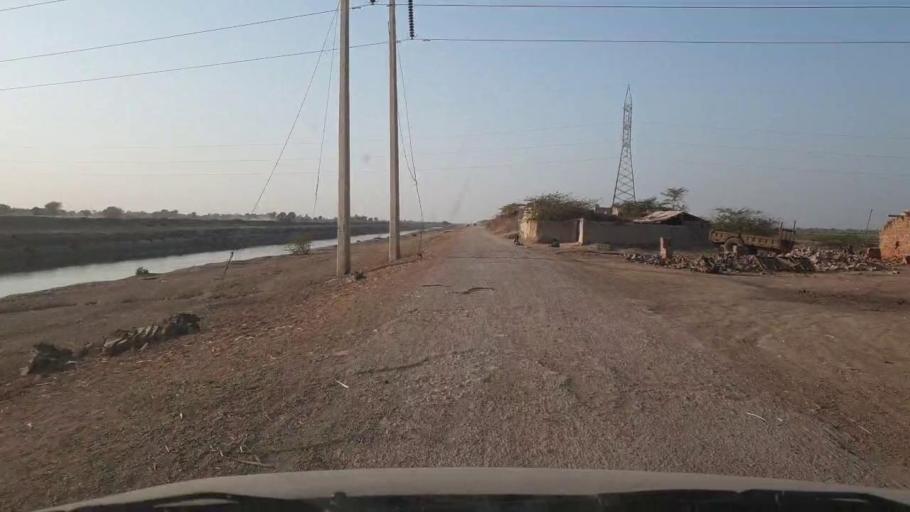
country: PK
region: Sindh
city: Samaro
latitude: 25.2801
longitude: 69.3412
